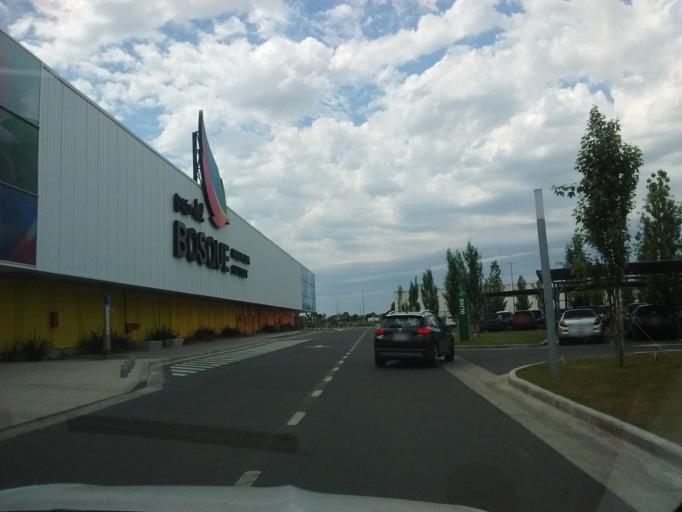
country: AR
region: Santa Fe
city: Granadero Baigorria
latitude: -32.9067
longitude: -60.7220
